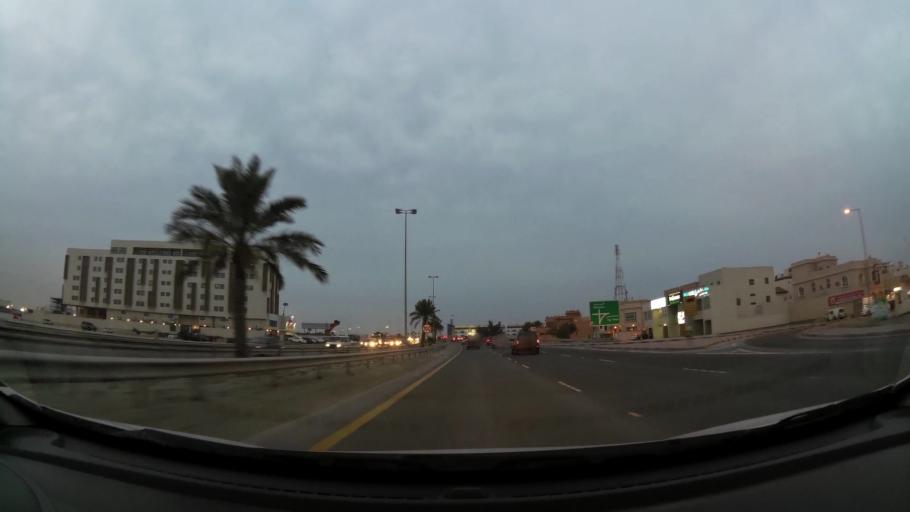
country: BH
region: Northern
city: Ar Rifa'
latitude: 26.1476
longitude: 50.5764
